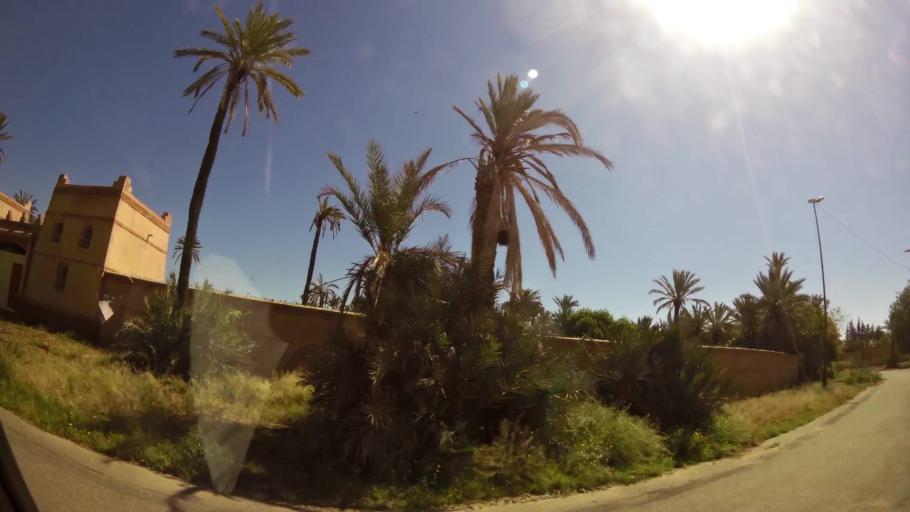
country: MA
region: Marrakech-Tensift-Al Haouz
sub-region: Marrakech
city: Marrakesh
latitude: 31.6537
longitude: -7.9650
